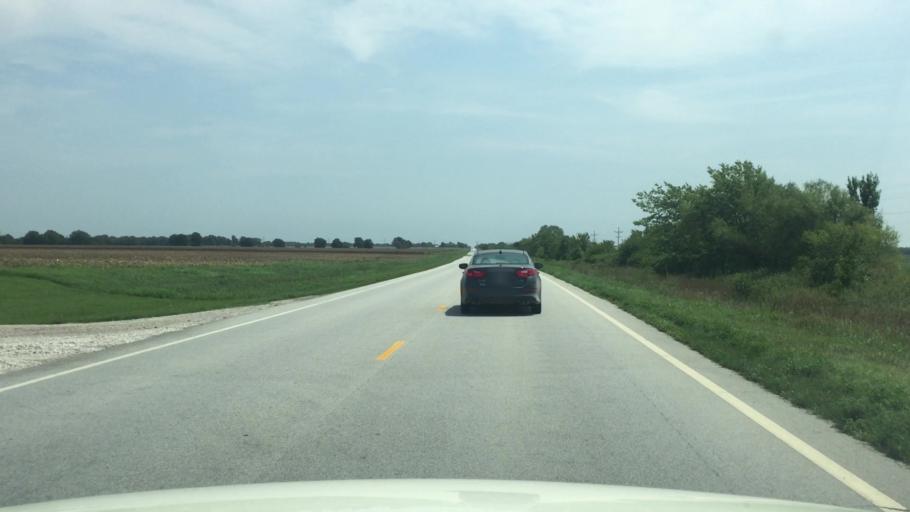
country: US
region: Kansas
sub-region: Cherokee County
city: Columbus
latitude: 37.1793
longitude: -94.9370
